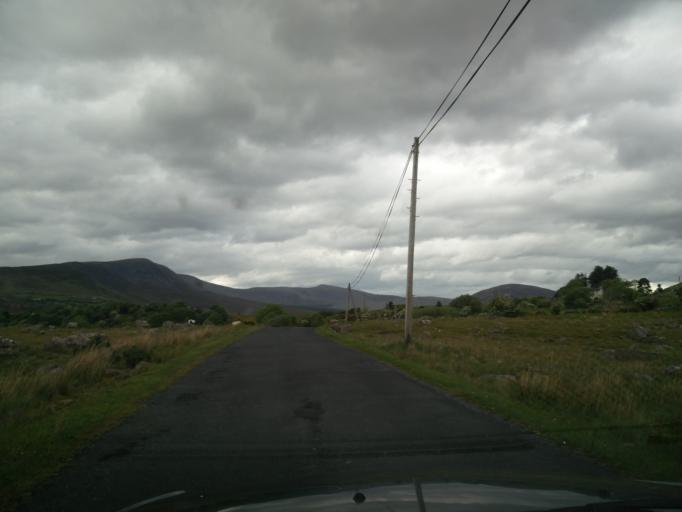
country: IE
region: Connaught
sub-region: Maigh Eo
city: Westport
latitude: 53.9231
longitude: -9.5612
